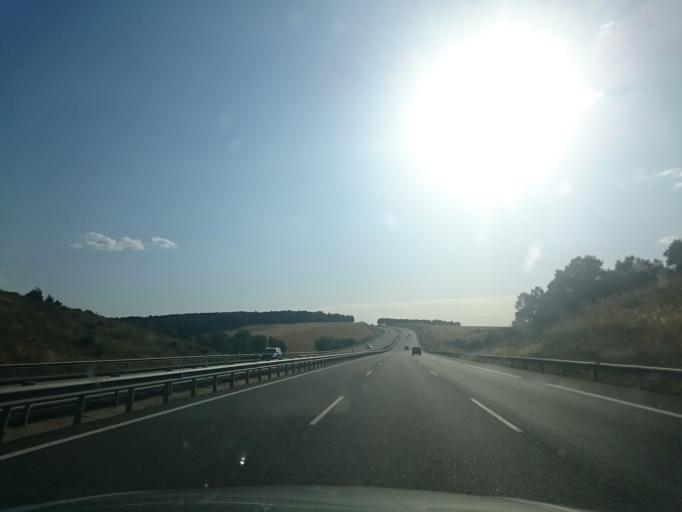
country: ES
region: Castille and Leon
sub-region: Provincia de Burgos
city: Cardenajimeno
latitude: 42.3307
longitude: -3.6390
